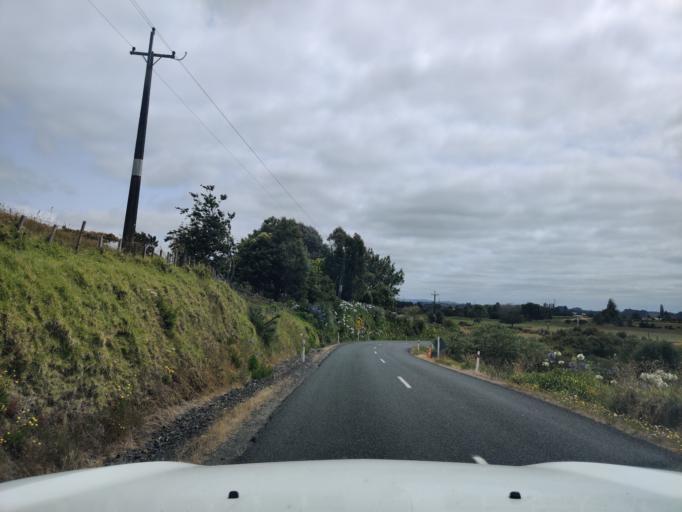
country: NZ
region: Waikato
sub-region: Waikato District
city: Te Kauwhata
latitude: -37.5256
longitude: 175.1714
